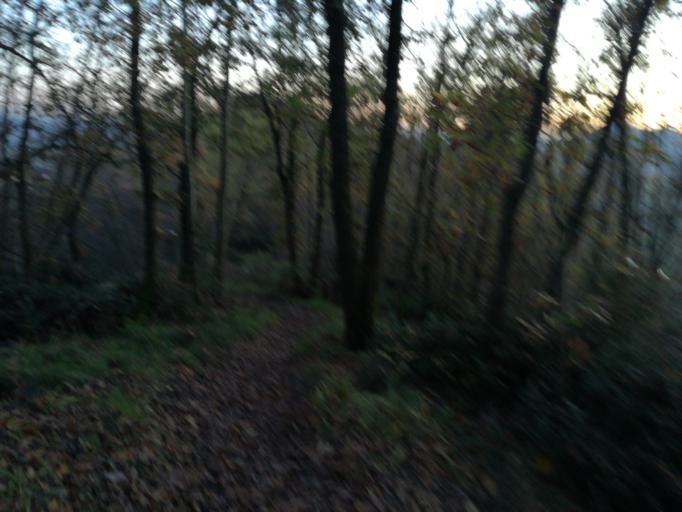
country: IT
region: Veneto
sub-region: Provincia di Padova
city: Battaglia Terme
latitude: 45.3001
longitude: 11.7673
